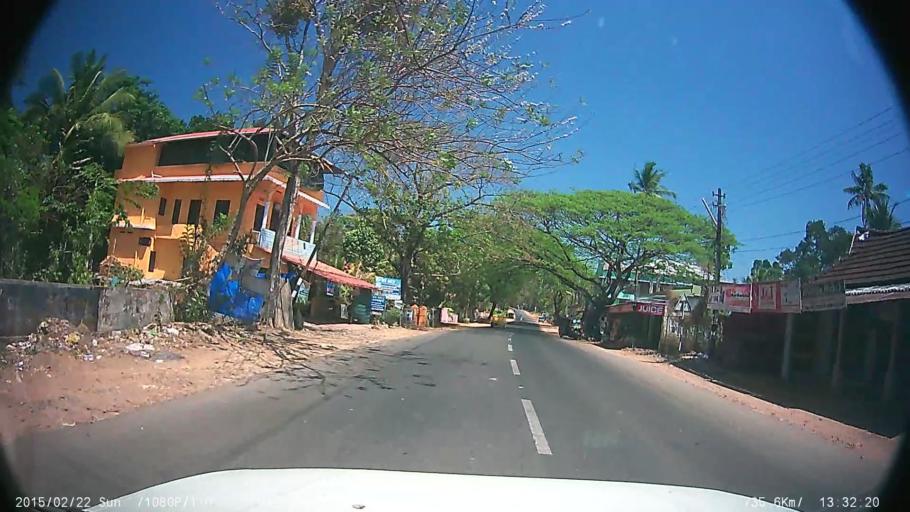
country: IN
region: Kerala
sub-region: Kottayam
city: Changanacheri
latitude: 9.4781
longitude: 76.5829
